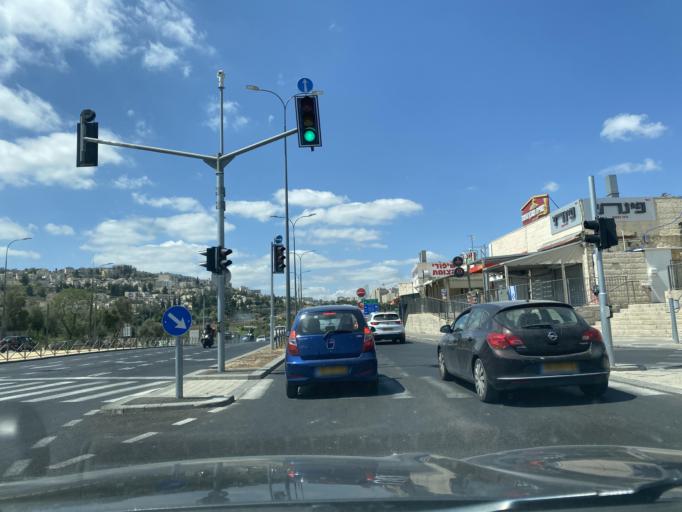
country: IL
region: Jerusalem
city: Jerusalem
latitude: 31.7560
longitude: 35.1986
